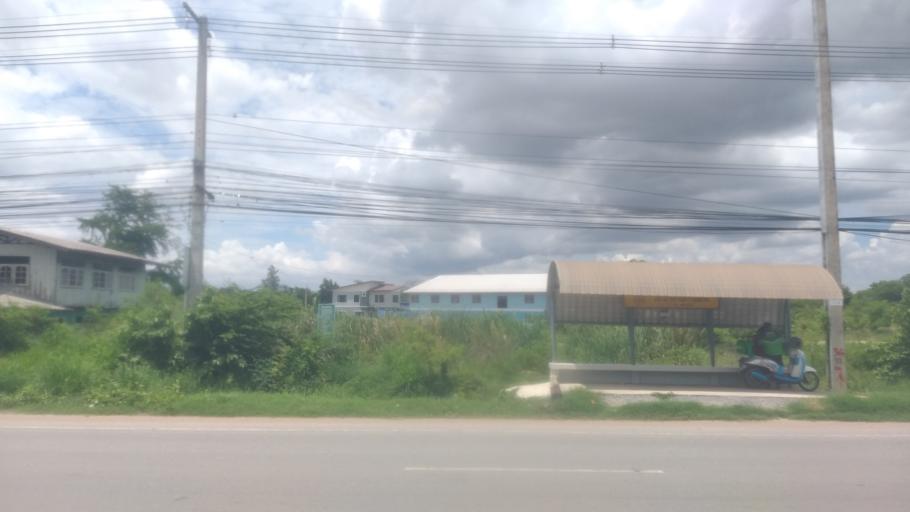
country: TH
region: Nakhon Ratchasima
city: Nakhon Ratchasima
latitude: 15.0764
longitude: 102.1166
